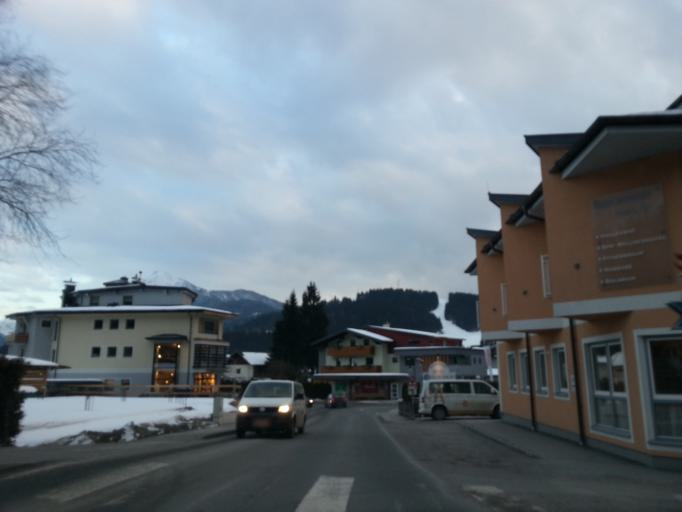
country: AT
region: Salzburg
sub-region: Politischer Bezirk Sankt Johann im Pongau
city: Altenmarkt im Pongau
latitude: 47.3863
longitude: 13.4138
